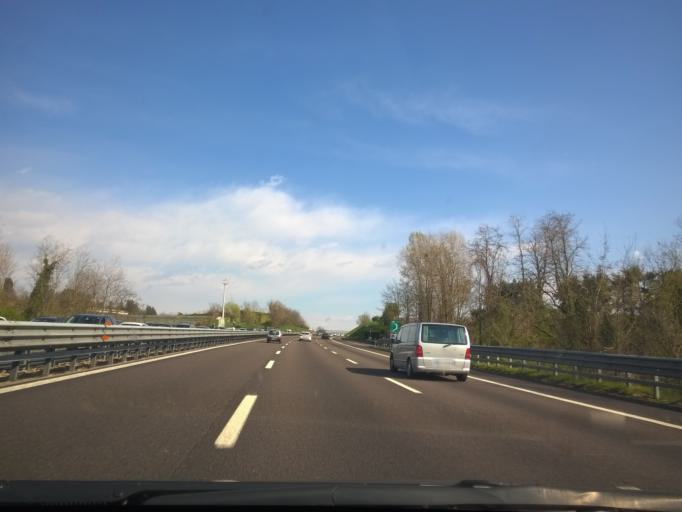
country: IT
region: Veneto
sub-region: Provincia di Verona
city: San Giorgio in Salici
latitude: 45.4241
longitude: 10.7745
